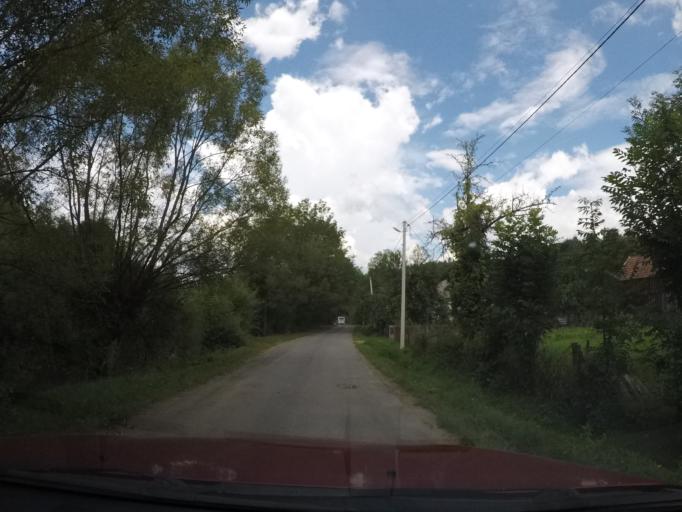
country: UA
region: Zakarpattia
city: Velykyi Bereznyi
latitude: 49.0188
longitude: 22.6183
